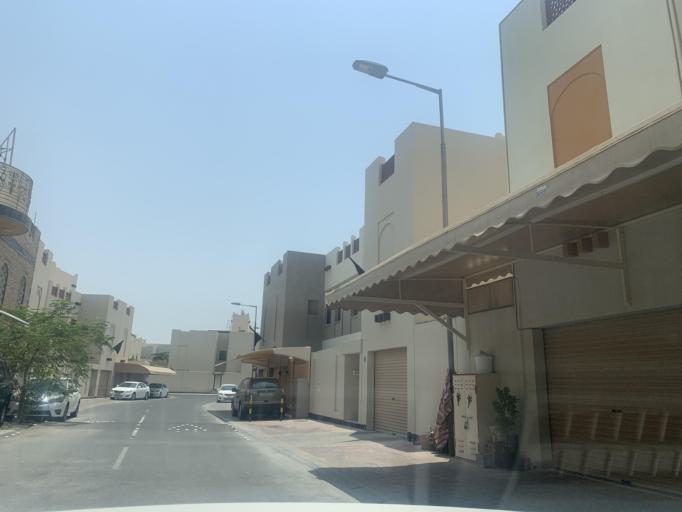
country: BH
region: Central Governorate
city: Madinat Hamad
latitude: 26.1456
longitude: 50.4633
